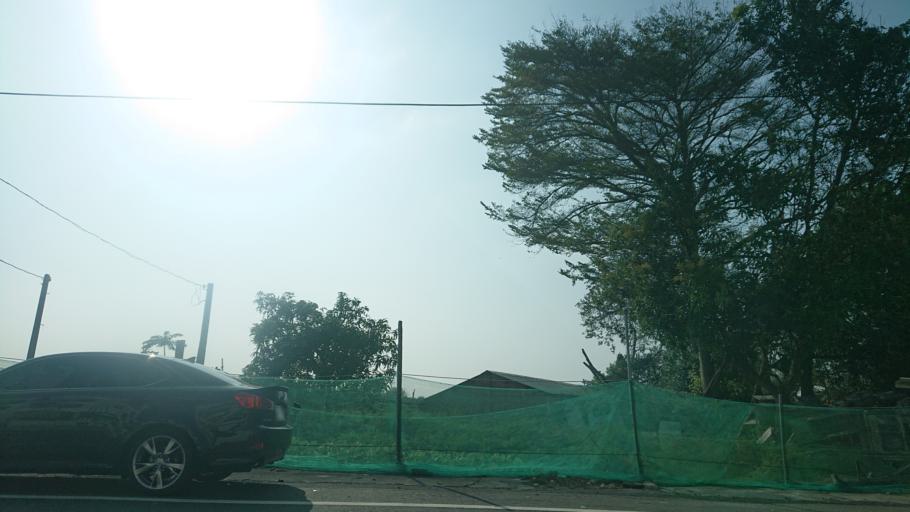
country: TW
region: Taiwan
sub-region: Chiayi
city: Taibao
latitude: 23.4581
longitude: 120.2410
